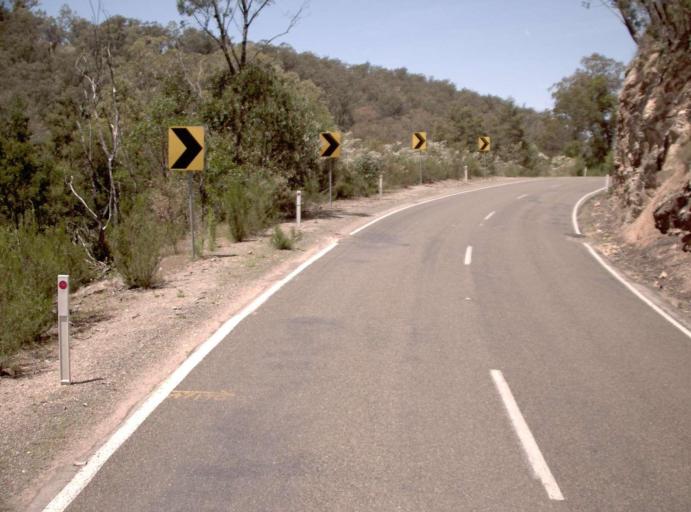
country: AU
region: Victoria
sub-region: East Gippsland
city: Bairnsdale
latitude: -37.4851
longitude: 147.8326
